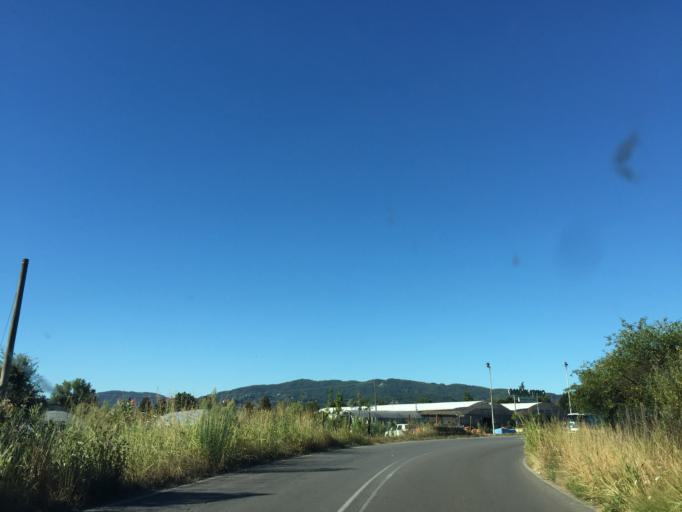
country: IT
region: Tuscany
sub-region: Provincia di Pistoia
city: Pistoia
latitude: 43.9315
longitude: 10.8950
